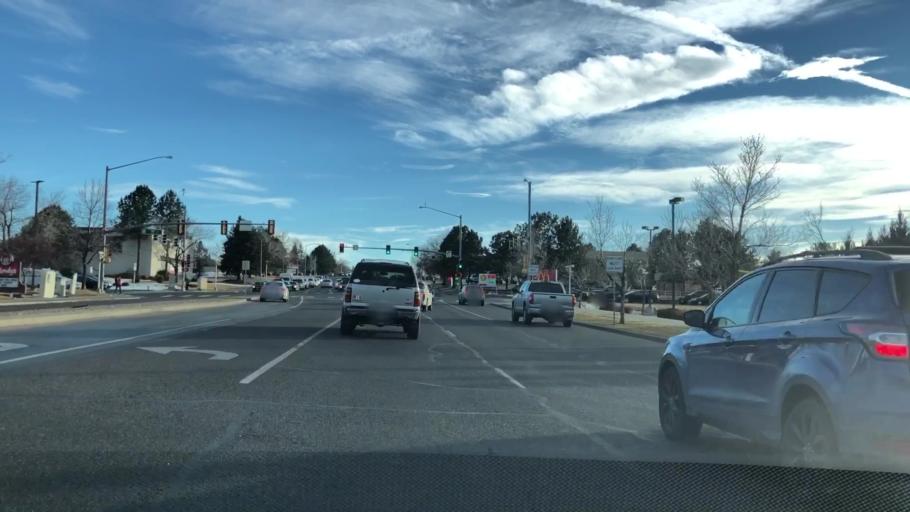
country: US
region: Colorado
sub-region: Adams County
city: Aurora
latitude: 39.6747
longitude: -104.7912
